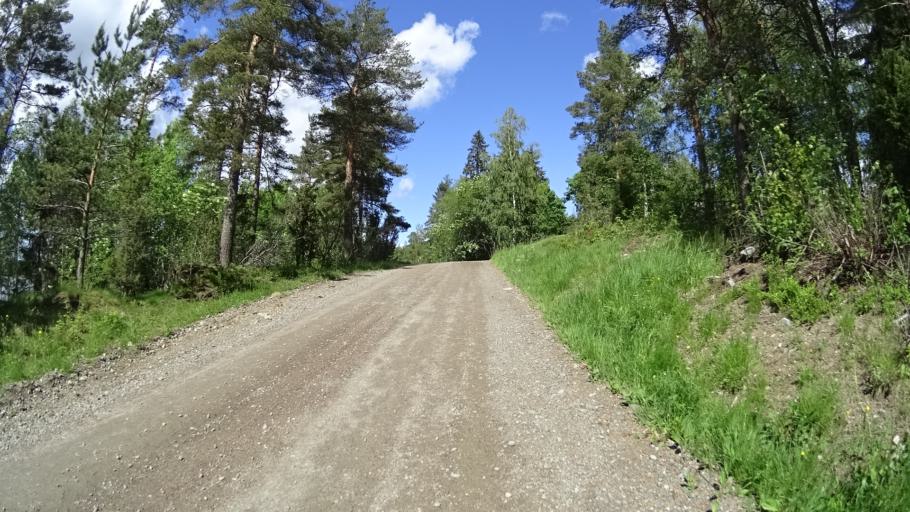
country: FI
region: Uusimaa
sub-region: Raaseporin
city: Karis
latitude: 60.1295
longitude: 23.6169
